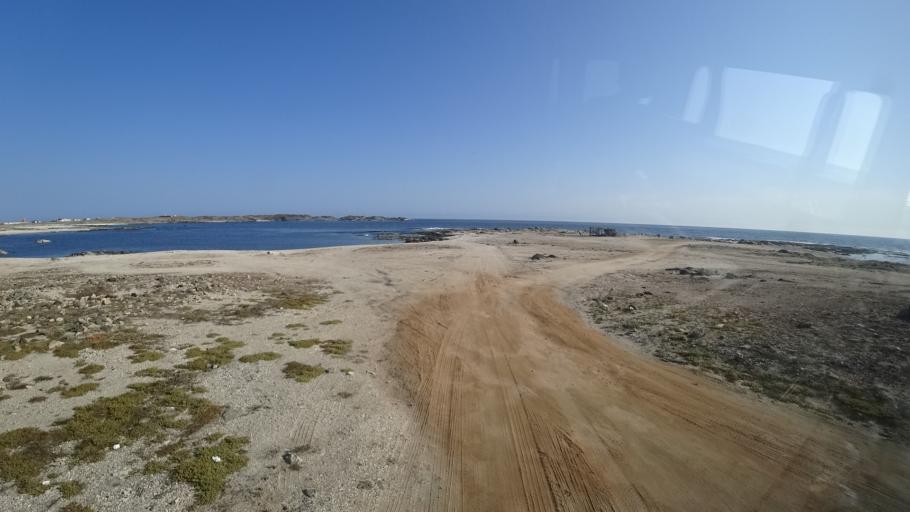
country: OM
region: Zufar
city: Salalah
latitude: 16.9460
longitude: 54.7921
